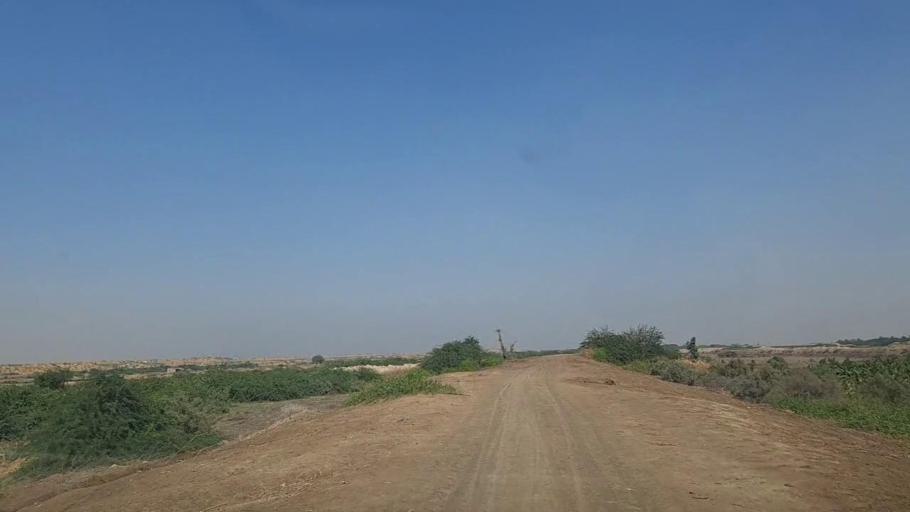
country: PK
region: Sindh
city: Thatta
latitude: 24.8427
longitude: 68.0223
